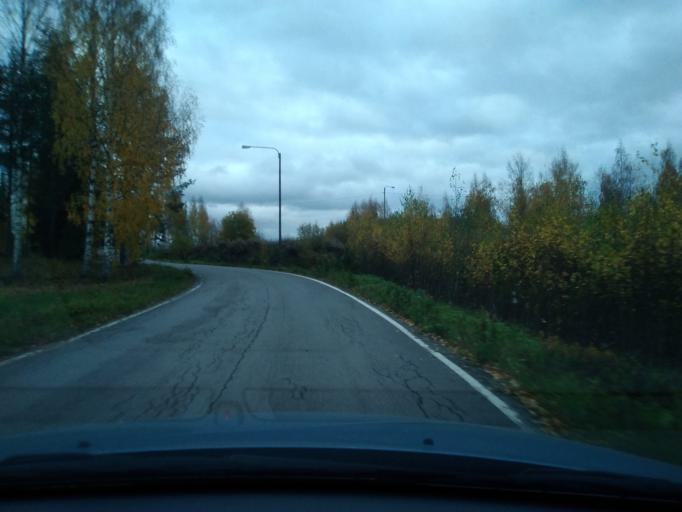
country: FI
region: Central Finland
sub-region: Saarijaervi-Viitasaari
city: Saarijaervi
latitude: 62.6884
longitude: 25.3185
